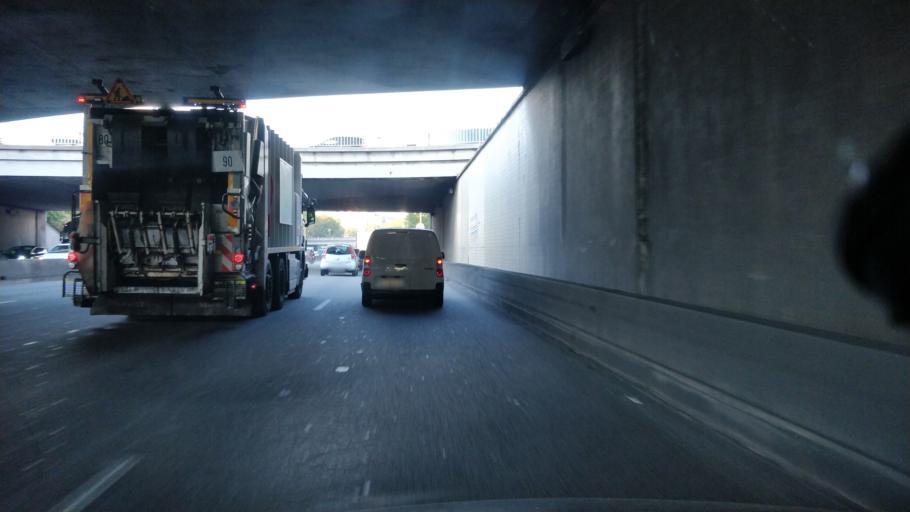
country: FR
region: Ile-de-France
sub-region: Departement du Val-de-Marne
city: Saint-Mande
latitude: 48.8466
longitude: 2.4147
